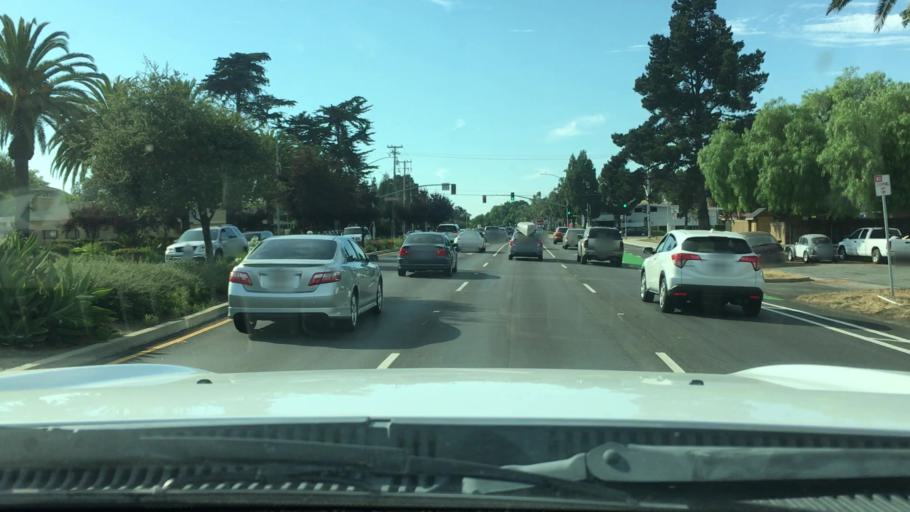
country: US
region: California
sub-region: San Luis Obispo County
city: San Luis Obispo
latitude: 35.2557
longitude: -120.6900
